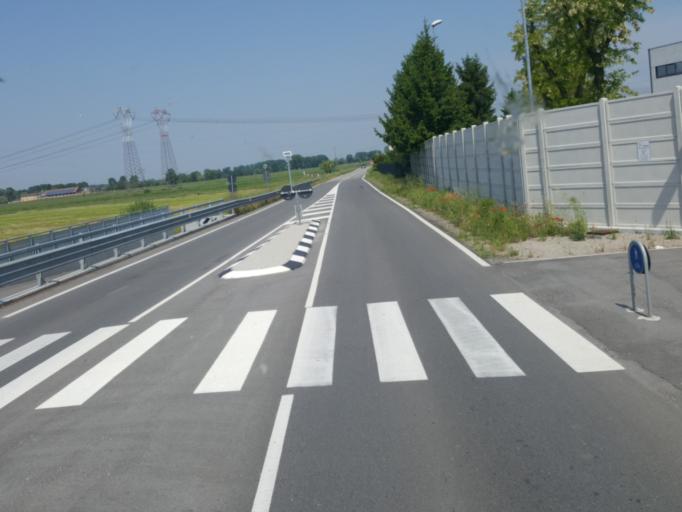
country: IT
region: Lombardy
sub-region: Provincia di Lodi
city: Boffalora d'Adda
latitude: 45.3421
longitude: 9.4991
